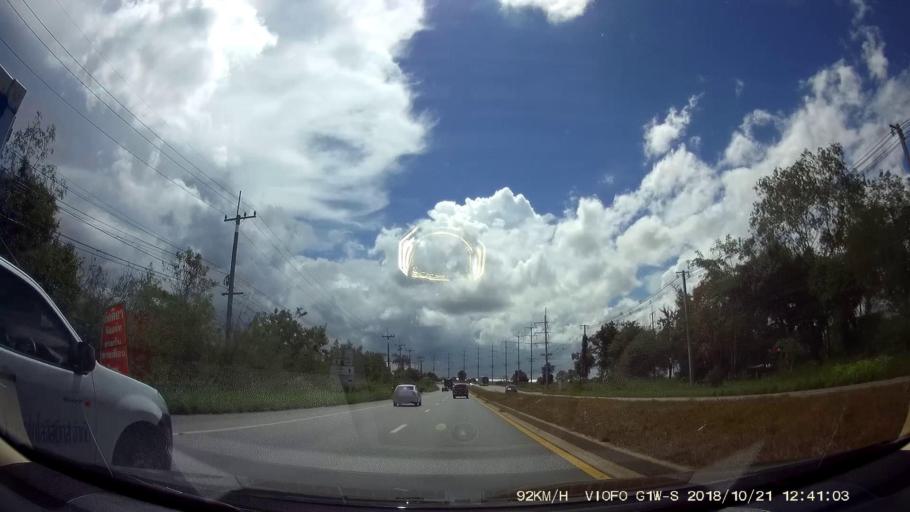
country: TH
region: Nakhon Ratchasima
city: Amphoe Sikhiu
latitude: 15.0173
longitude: 101.6885
